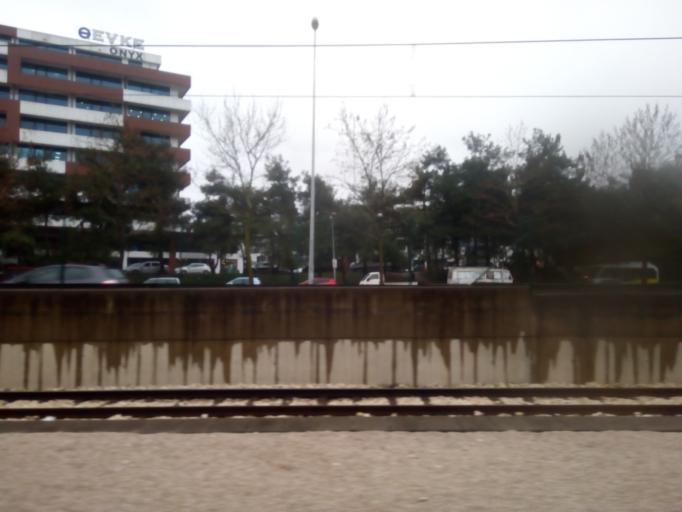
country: TR
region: Bursa
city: Yildirim
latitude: 40.2295
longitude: 28.9862
